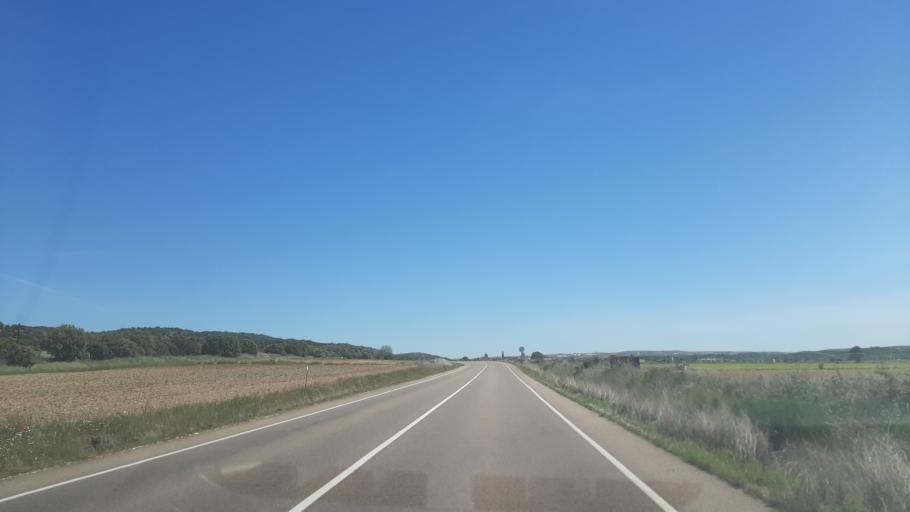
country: ES
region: Castille and Leon
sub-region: Provincia de Salamanca
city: Encinas de Arriba
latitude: 40.7868
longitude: -5.5513
